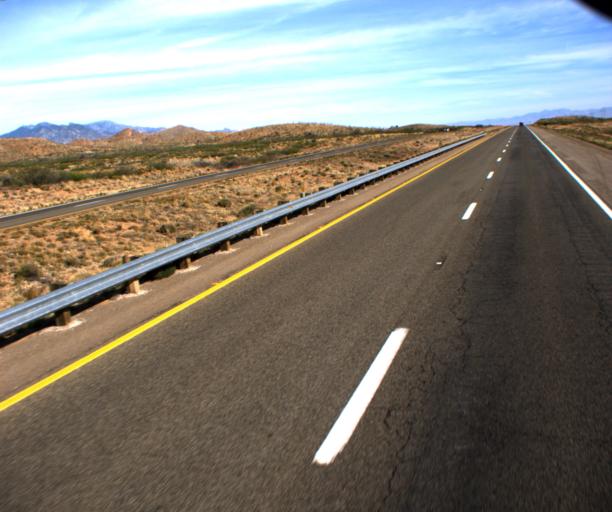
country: US
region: Arizona
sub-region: Graham County
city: Swift Trail Junction
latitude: 32.4979
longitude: -109.6736
